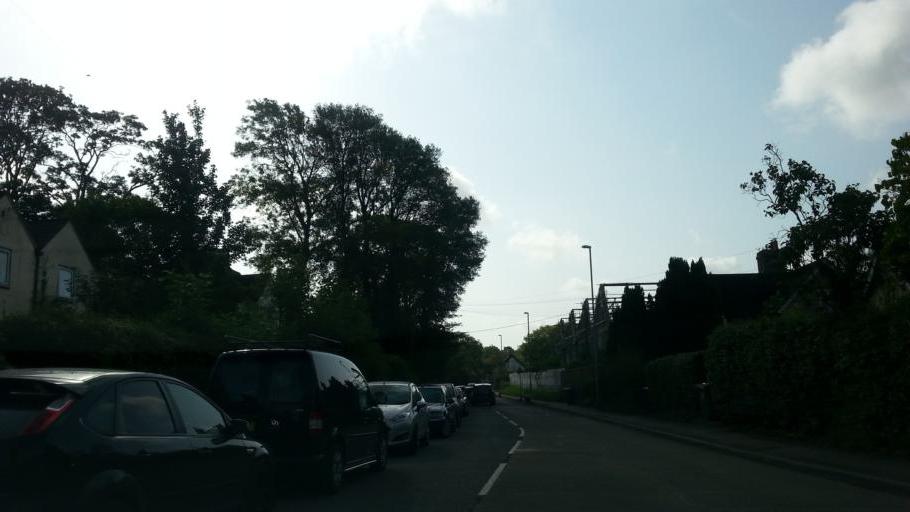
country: GB
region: England
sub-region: Cambridgeshire
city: Papworth Everard
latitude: 52.2490
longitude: -0.1177
